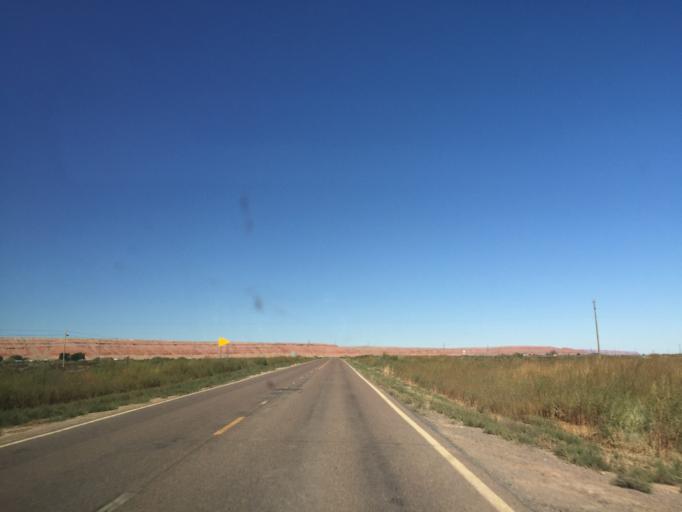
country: US
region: Arizona
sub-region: Apache County
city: Many Farms
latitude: 36.3309
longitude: -109.6221
